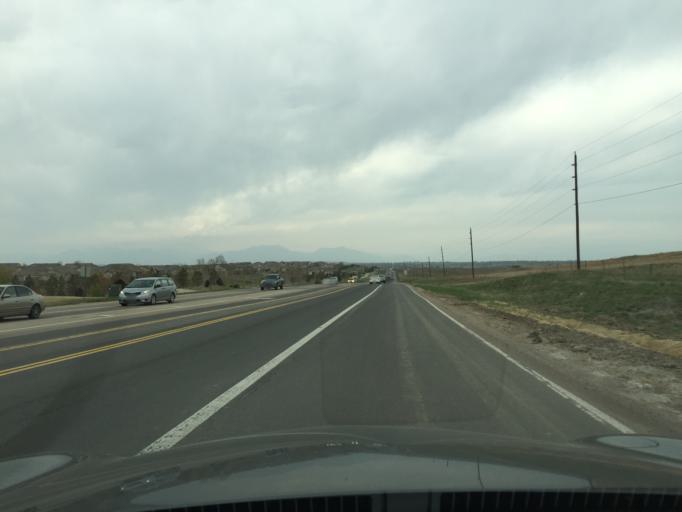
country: US
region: Colorado
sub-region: Boulder County
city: Erie
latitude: 40.0003
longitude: -105.0372
